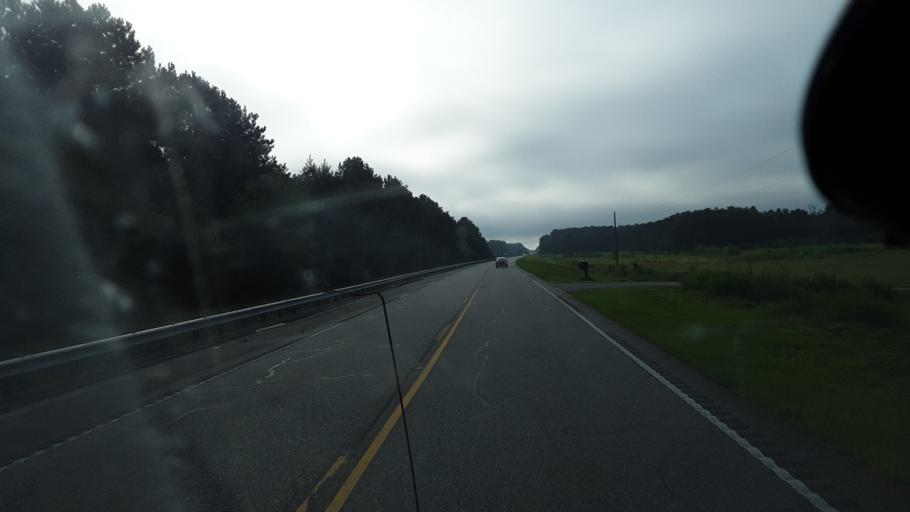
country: US
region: South Carolina
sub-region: Horry County
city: Red Hill
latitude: 33.8492
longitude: -79.2928
